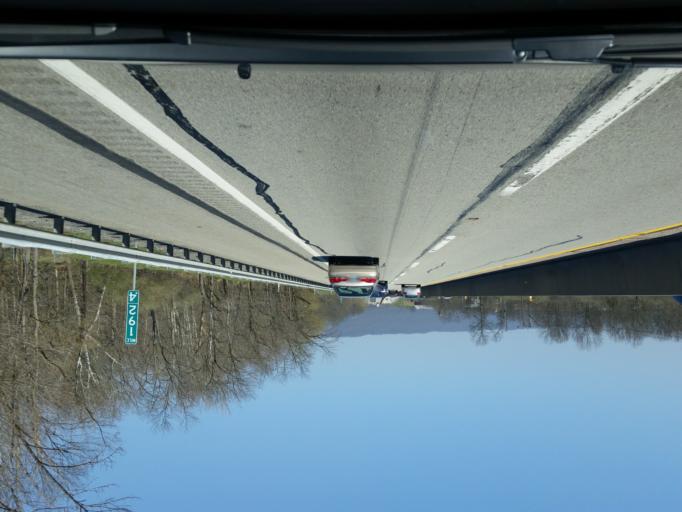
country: US
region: Pennsylvania
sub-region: Franklin County
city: Doylestown
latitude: 40.1262
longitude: -77.7525
